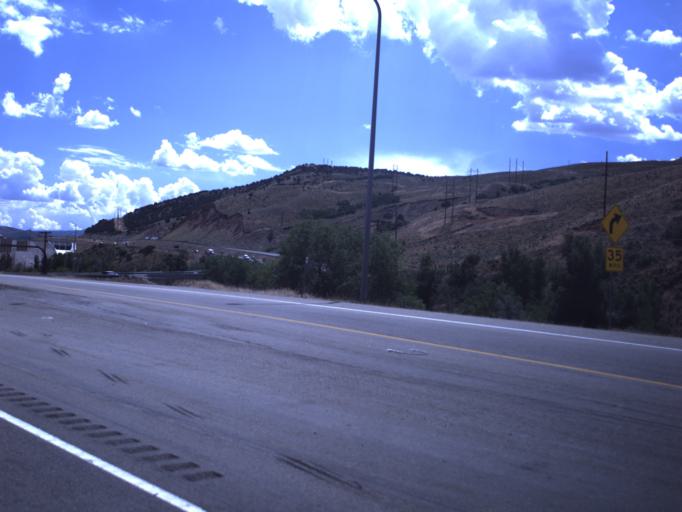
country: US
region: Utah
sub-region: Summit County
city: Coalville
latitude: 40.9705
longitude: -111.4411
